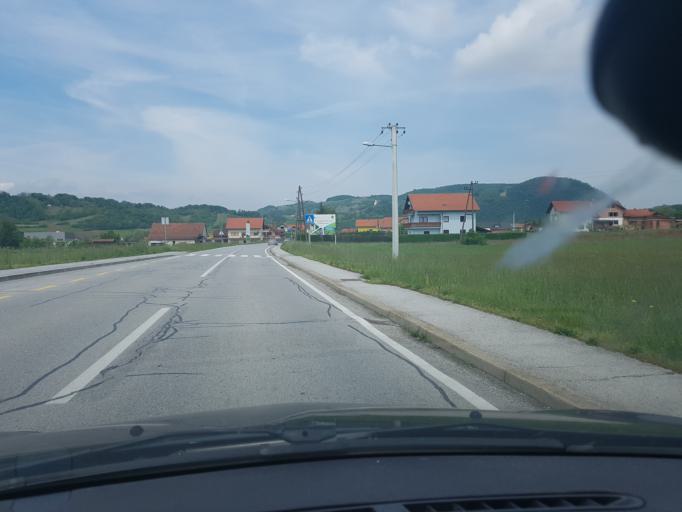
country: HR
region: Krapinsko-Zagorska
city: Pregrada
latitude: 46.1477
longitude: 15.7637
